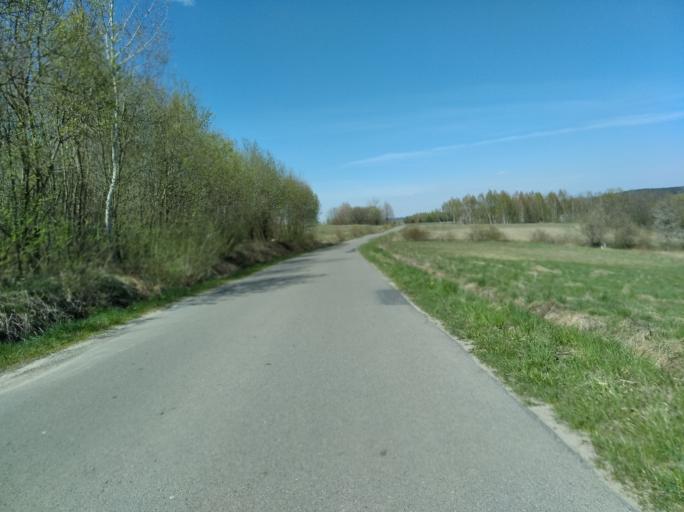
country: PL
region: Subcarpathian Voivodeship
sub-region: Powiat brzozowski
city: Jablonka
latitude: 49.7366
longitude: 22.1147
